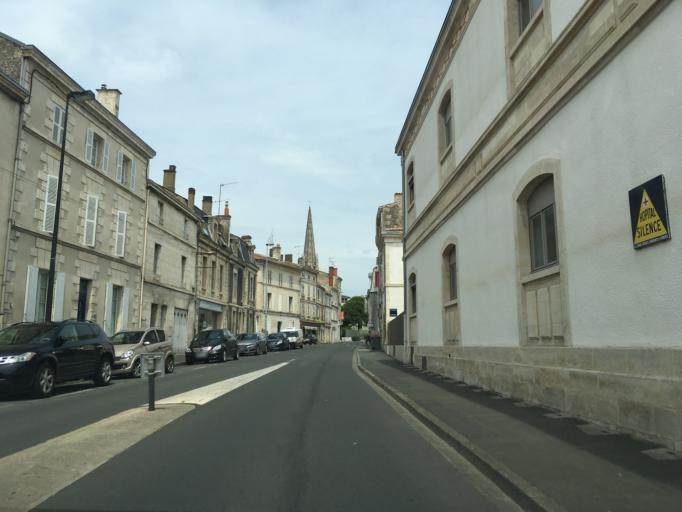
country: FR
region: Poitou-Charentes
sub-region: Departement des Deux-Sevres
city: Niort
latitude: 46.3198
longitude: -0.4656
